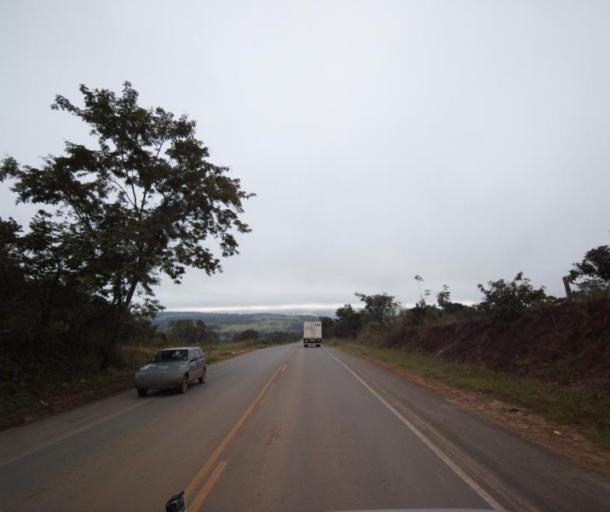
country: BR
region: Goias
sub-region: Pirenopolis
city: Pirenopolis
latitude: -15.9570
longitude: -48.8111
